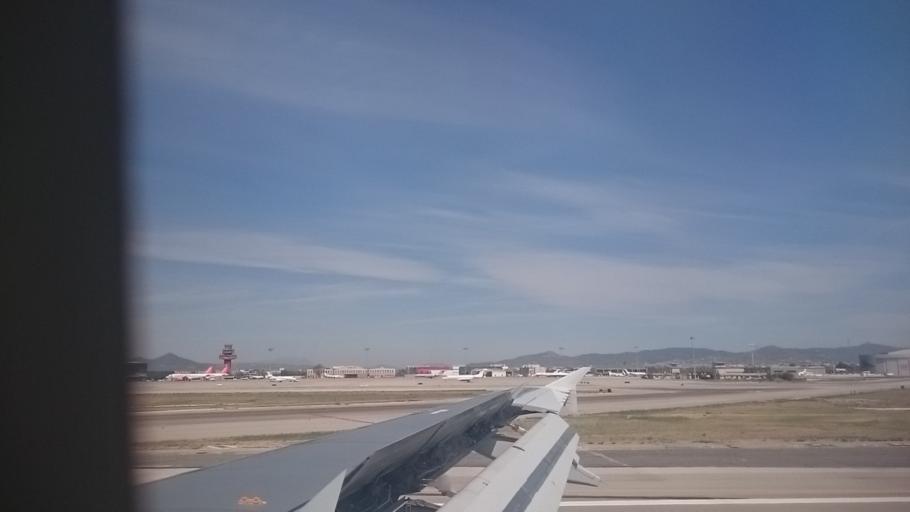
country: ES
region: Catalonia
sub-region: Provincia de Barcelona
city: El Prat de Llobregat
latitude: 41.3009
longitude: 2.0890
